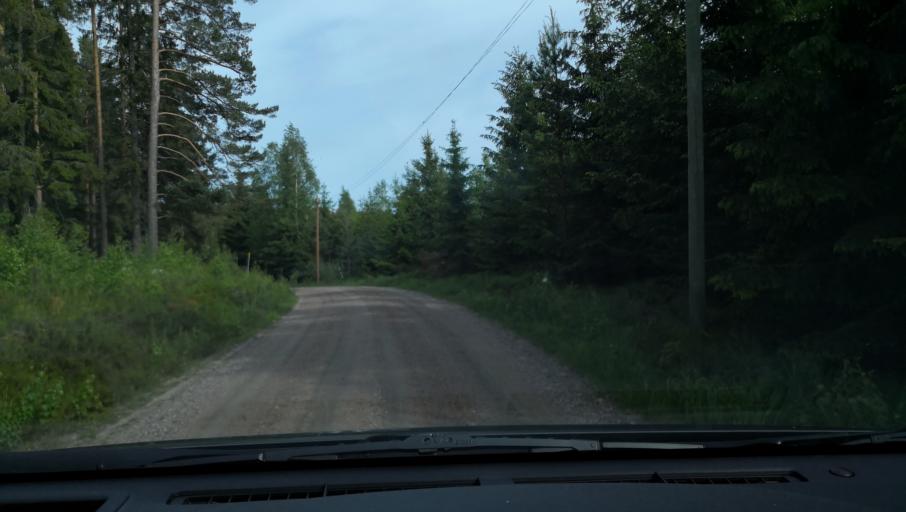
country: SE
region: Vaestmanland
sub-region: Arboga Kommun
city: Tyringe
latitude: 59.3649
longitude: 15.9976
